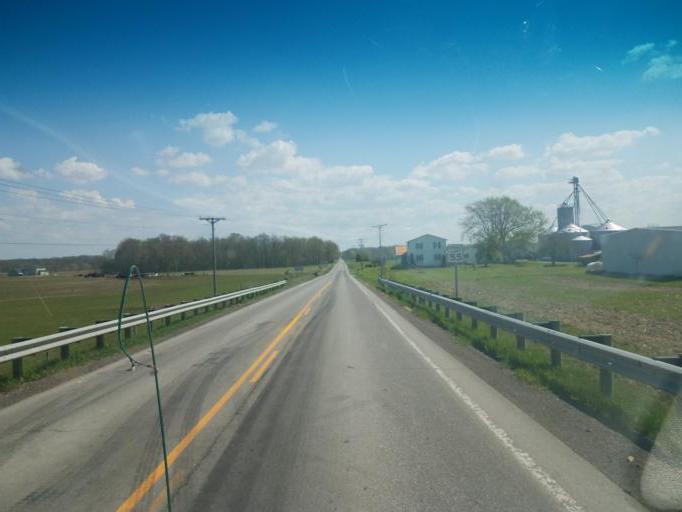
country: US
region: Ohio
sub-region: Wayne County
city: West Salem
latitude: 40.9334
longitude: -82.1092
